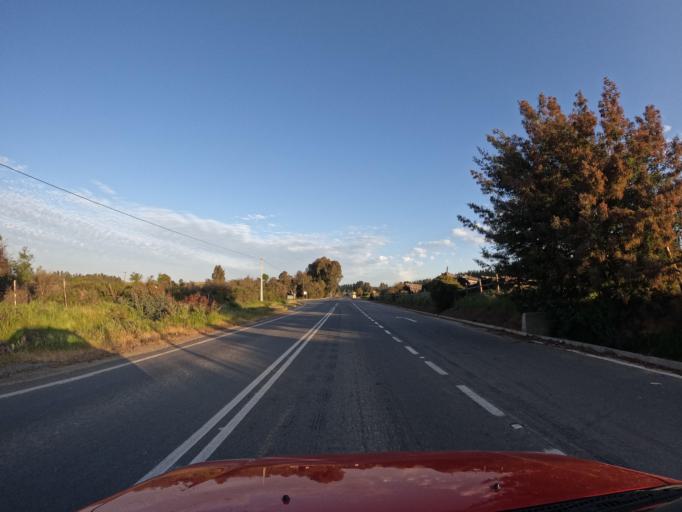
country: CL
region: O'Higgins
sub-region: Provincia de Colchagua
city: Santa Cruz
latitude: -34.3410
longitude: -71.7417
